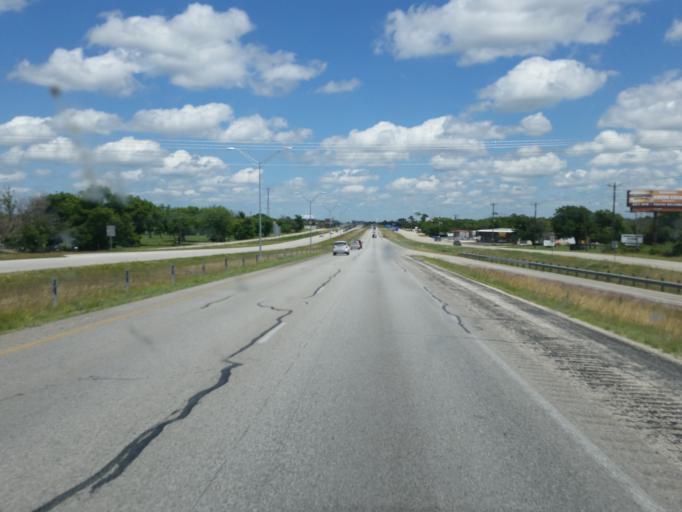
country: US
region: Texas
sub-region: Callahan County
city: Clyde
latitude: 32.4146
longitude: -99.5052
